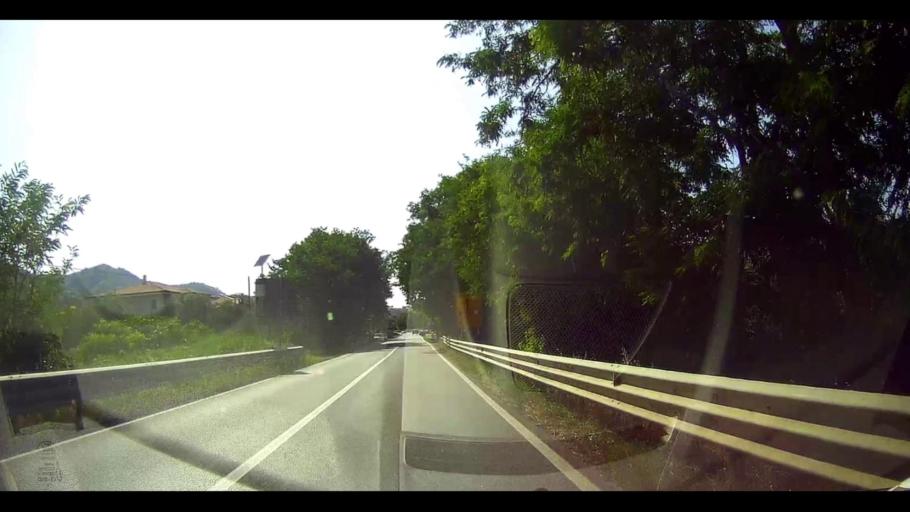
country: IT
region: Calabria
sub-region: Provincia di Cosenza
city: Cariati
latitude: 39.4835
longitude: 16.9755
